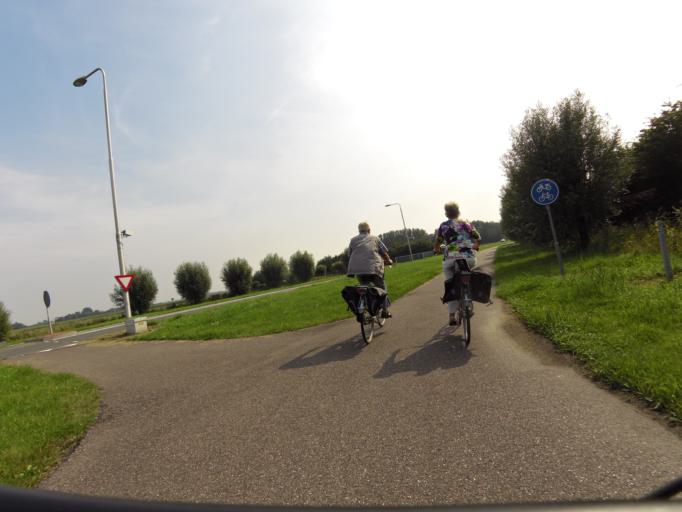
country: NL
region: Zeeland
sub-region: Gemeente Middelburg
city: Middelburg
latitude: 51.5425
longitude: 3.6023
